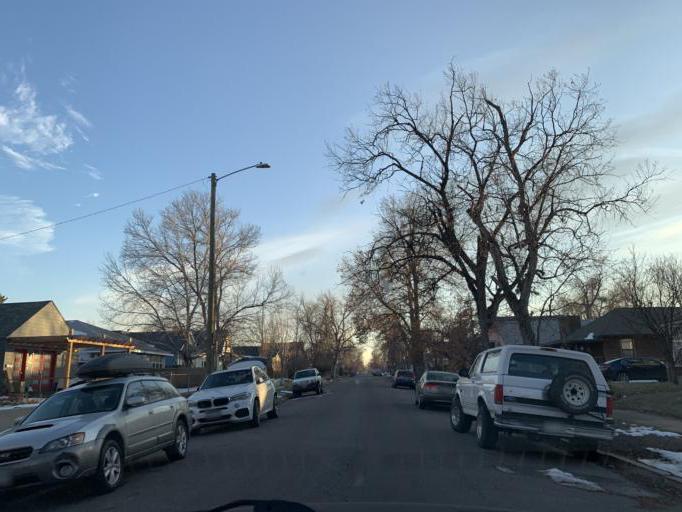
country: US
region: Colorado
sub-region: Adams County
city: Berkley
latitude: 39.7885
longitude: -105.0381
